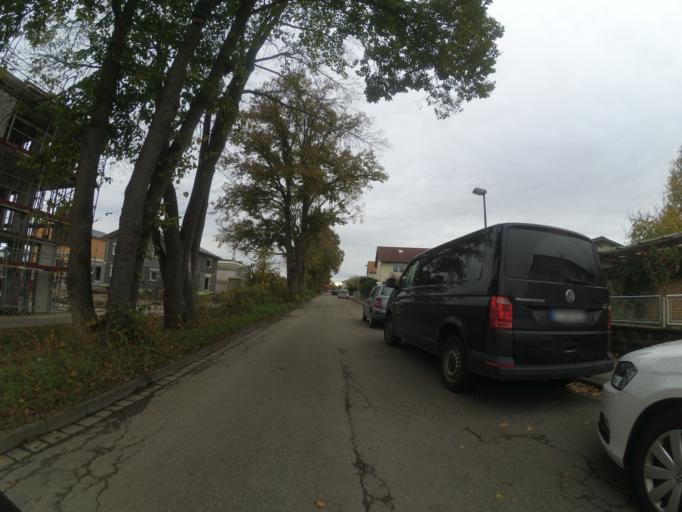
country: DE
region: Bavaria
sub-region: Swabia
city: Neu-Ulm
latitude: 48.3693
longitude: 10.0178
